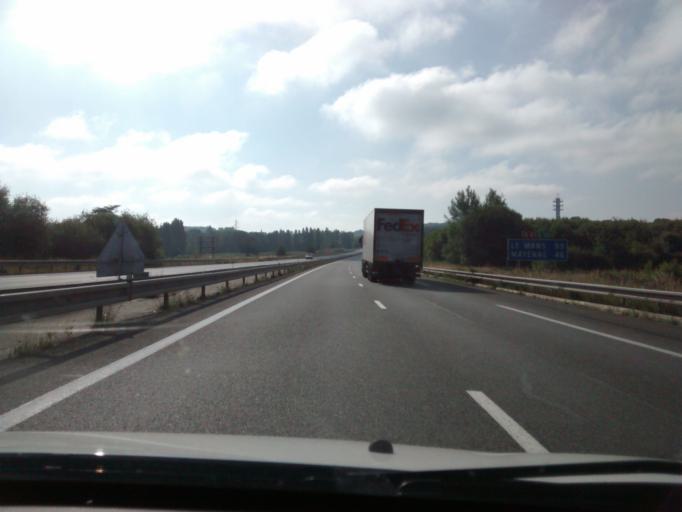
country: FR
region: Pays de la Loire
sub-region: Departement de la Mayenne
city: Saint-Pierre-la-Cour
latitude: 48.0817
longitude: -1.0090
